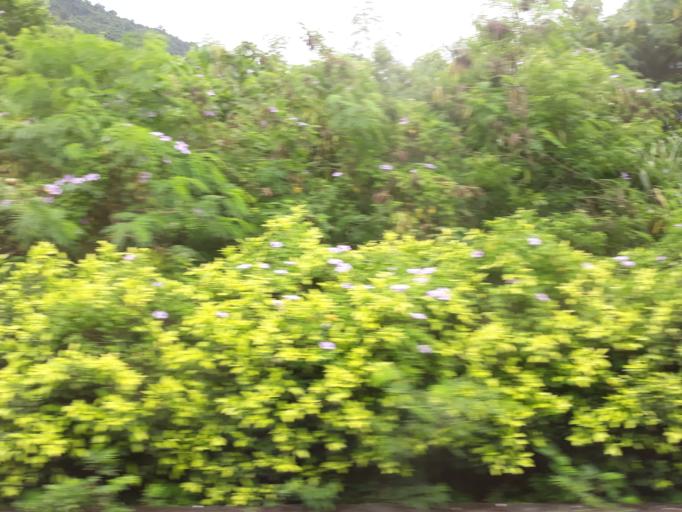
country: TW
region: Taiwan
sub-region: Yilan
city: Yilan
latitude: 24.4378
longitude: 121.7810
